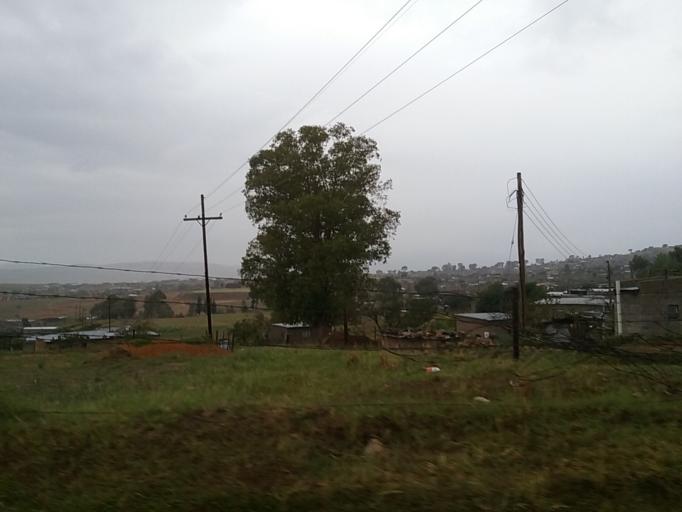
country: LS
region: Berea
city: Teyateyaneng
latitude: -29.1276
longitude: 27.7442
